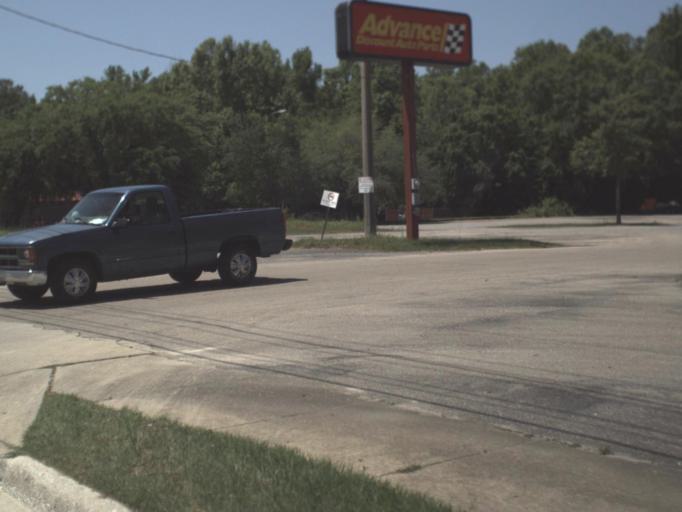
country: US
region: Florida
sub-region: Jefferson County
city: Monticello
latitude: 30.5338
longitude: -83.8703
